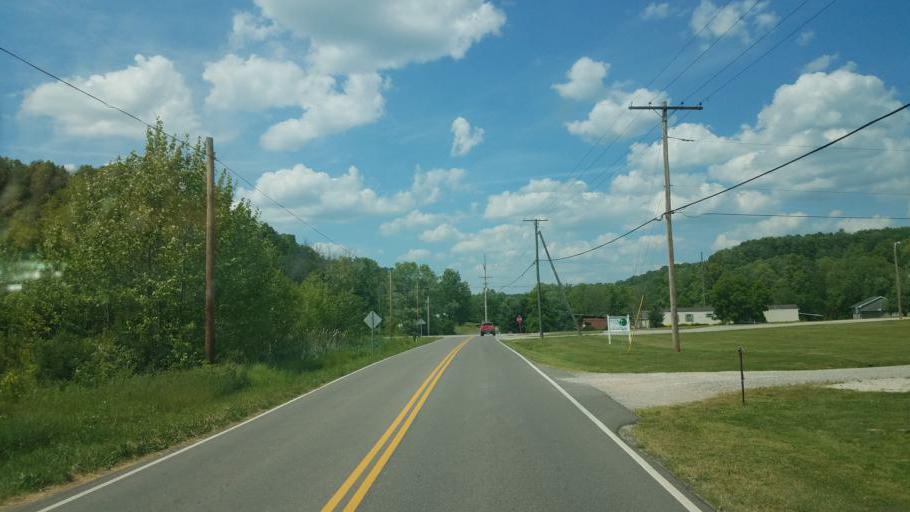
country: US
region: Ohio
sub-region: Meigs County
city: Middleport
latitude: 39.0262
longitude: -82.0853
